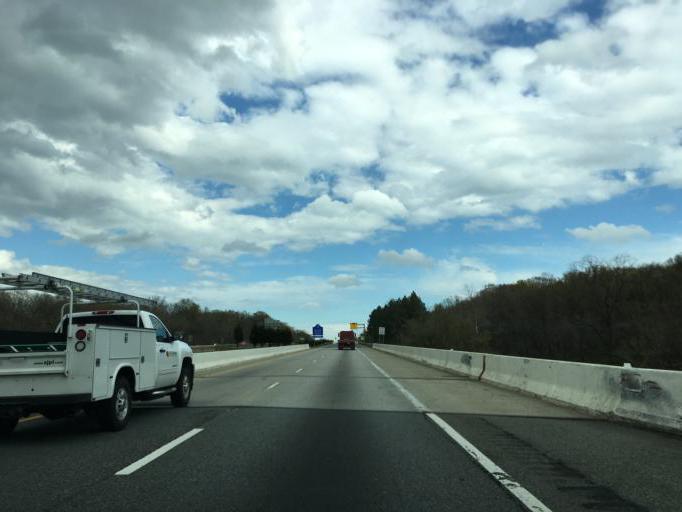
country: US
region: Maryland
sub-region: Anne Arundel County
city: Brooklyn Park
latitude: 39.2065
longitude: -76.6014
